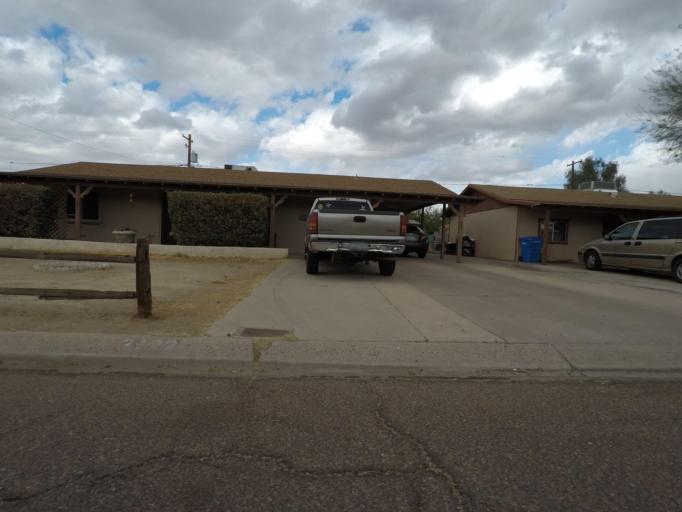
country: US
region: Arizona
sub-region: Maricopa County
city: Glendale
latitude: 33.4986
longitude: -112.1267
